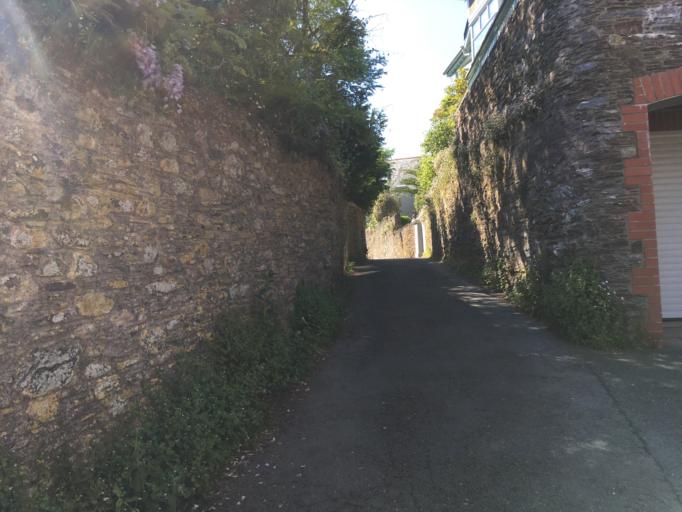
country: GB
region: England
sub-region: Devon
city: Dartmouth
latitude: 50.3473
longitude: -3.5715
